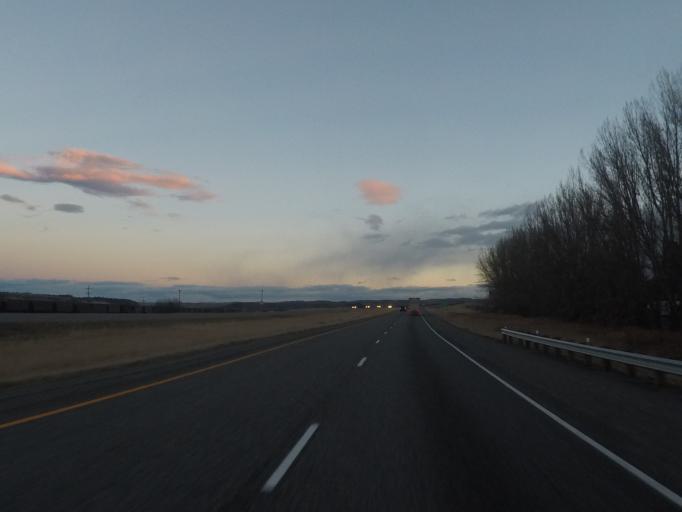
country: US
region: Montana
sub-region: Sweet Grass County
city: Big Timber
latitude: 45.7752
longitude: -109.7993
